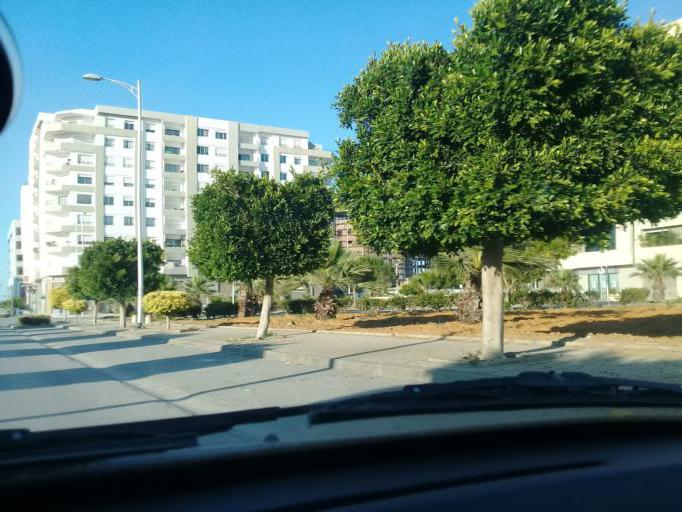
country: TN
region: Tunis
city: La Goulette
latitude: 36.8456
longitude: 10.2789
